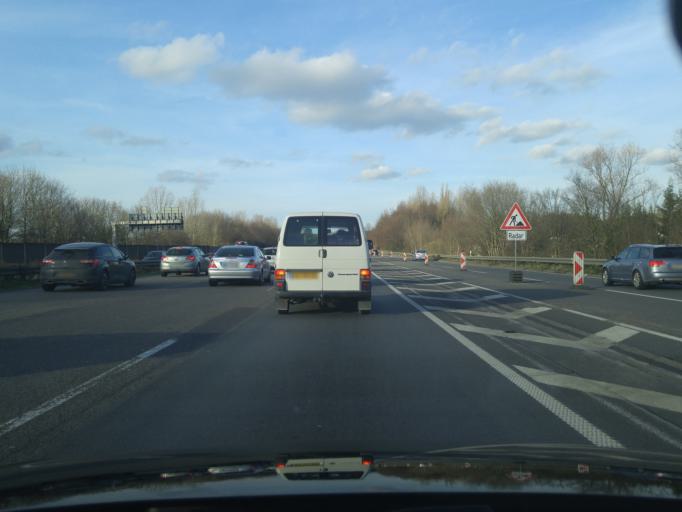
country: DE
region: North Rhine-Westphalia
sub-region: Regierungsbezirk Dusseldorf
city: Hilden
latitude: 51.1982
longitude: 6.9376
